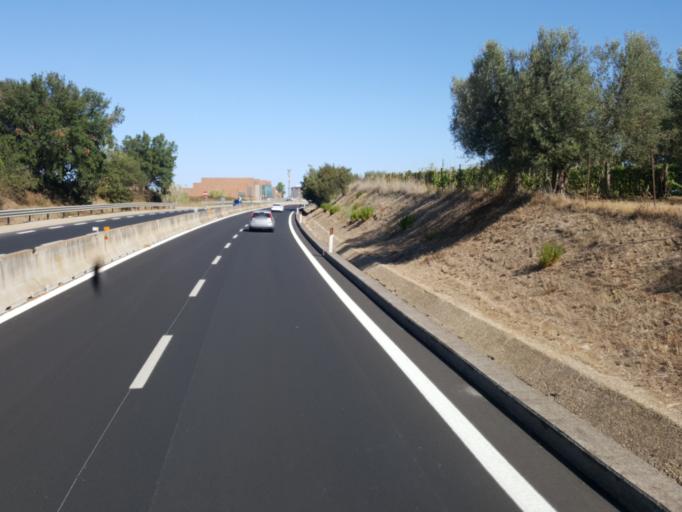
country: IT
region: Latium
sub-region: Provincia di Viterbo
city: Montalto di Castro
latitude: 42.3380
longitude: 11.6202
